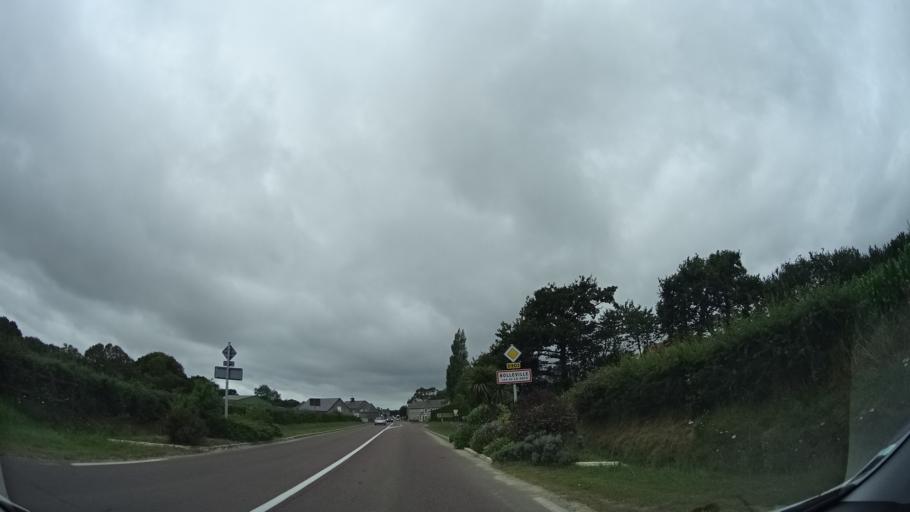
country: FR
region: Lower Normandy
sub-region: Departement de la Manche
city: La Haye-du-Puits
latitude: 49.3000
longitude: -1.5705
